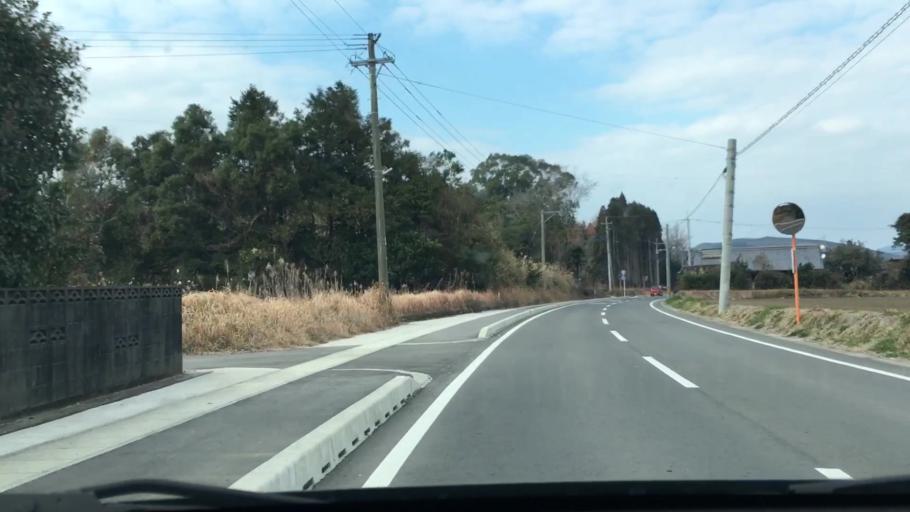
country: JP
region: Miyazaki
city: Kushima
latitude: 31.5213
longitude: 131.2370
